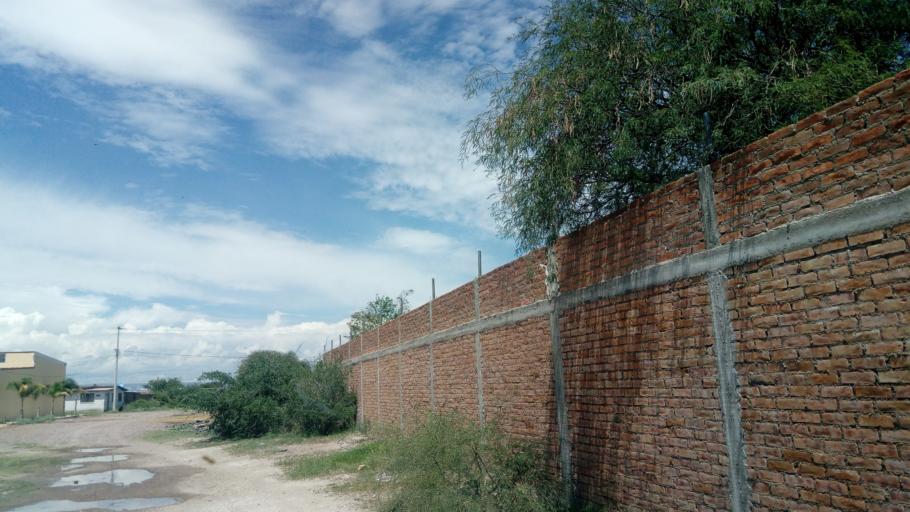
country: MX
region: Durango
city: Victoria de Durango
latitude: 24.0147
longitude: -104.5889
